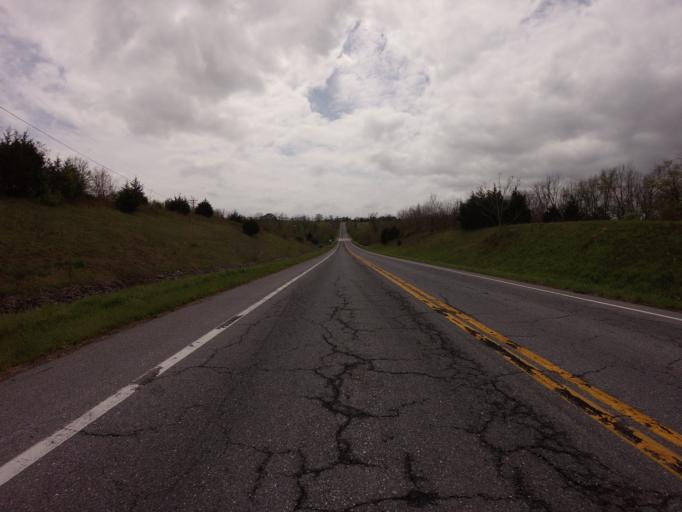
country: US
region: Maryland
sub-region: Frederick County
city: Woodsboro
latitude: 39.5551
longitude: -77.3735
